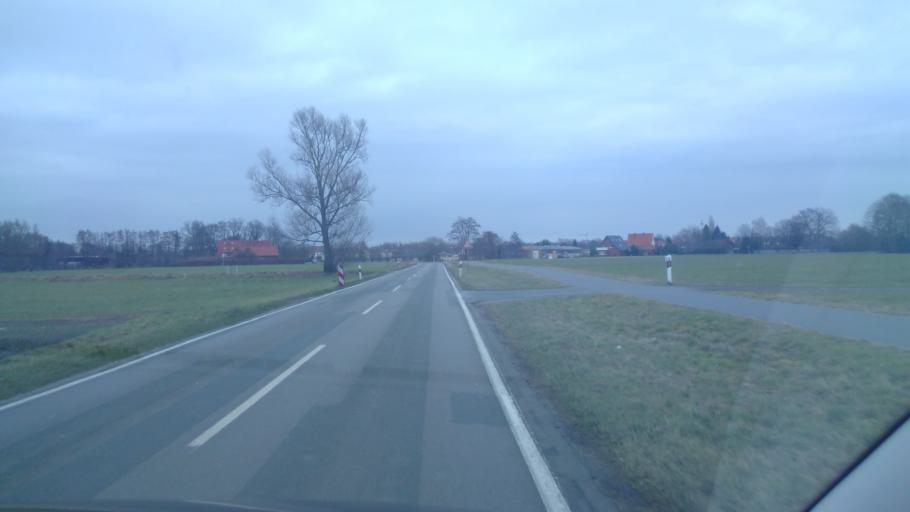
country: DE
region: North Rhine-Westphalia
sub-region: Regierungsbezirk Detmold
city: Verl
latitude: 51.8511
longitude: 8.5520
